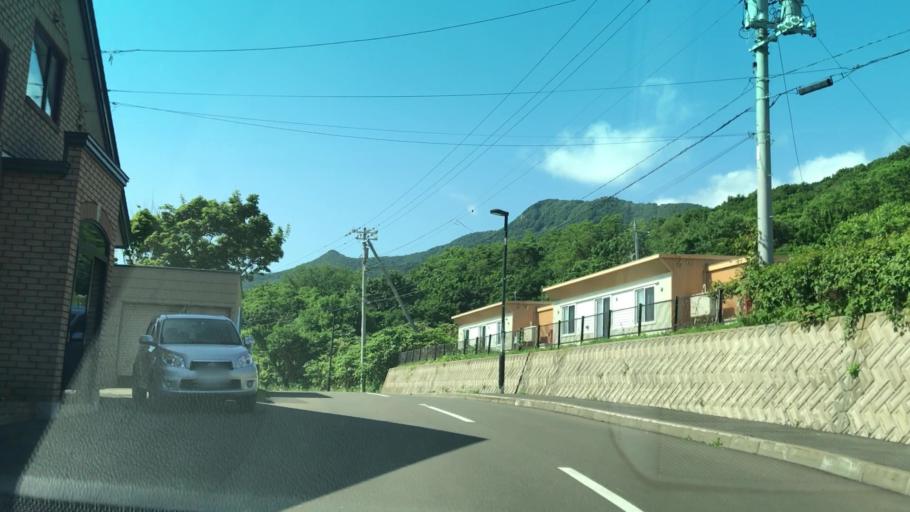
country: JP
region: Hokkaido
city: Iwanai
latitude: 43.1462
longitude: 140.4232
